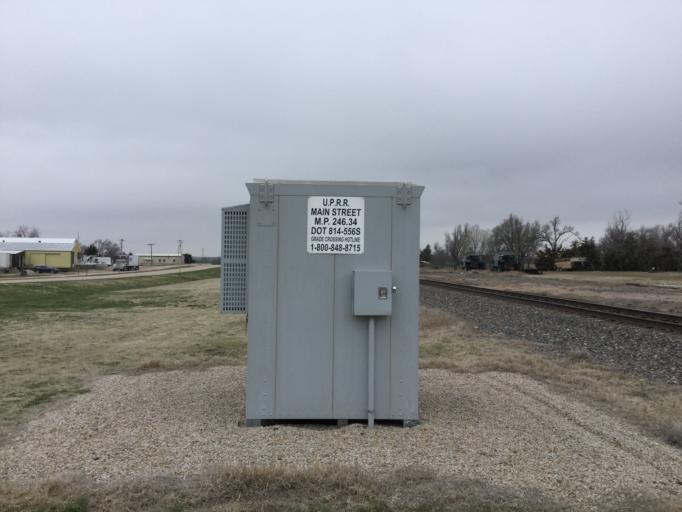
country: US
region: Kansas
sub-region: Russell County
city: Russell
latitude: 38.8471
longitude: -98.5893
